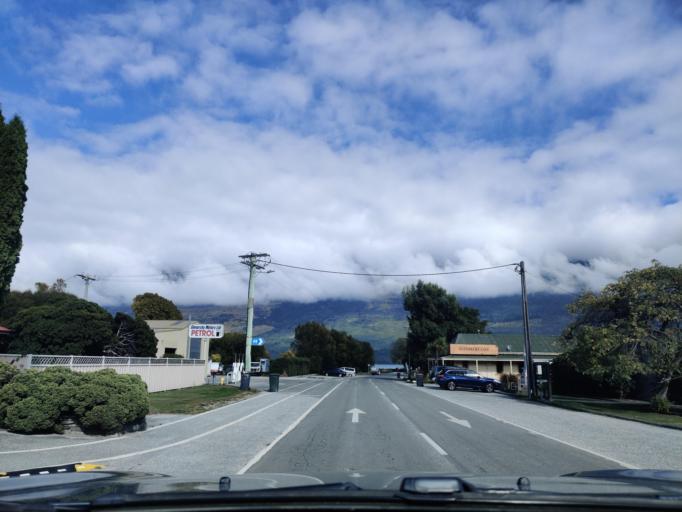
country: NZ
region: Otago
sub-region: Queenstown-Lakes District
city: Queenstown
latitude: -44.8498
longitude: 168.3848
